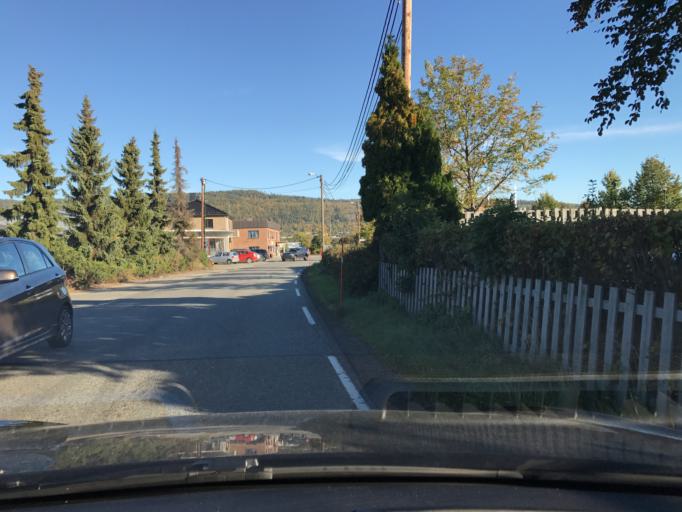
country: NO
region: Buskerud
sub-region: Lier
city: Lierbyen
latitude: 59.7657
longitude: 10.2579
